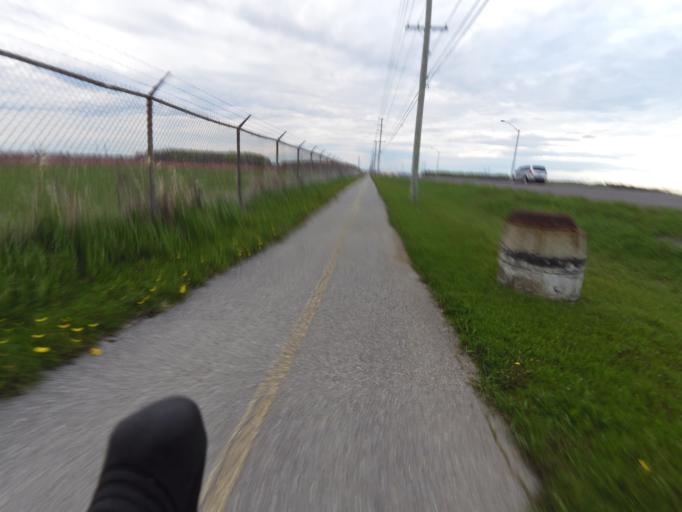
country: CA
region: Ontario
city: Bells Corners
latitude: 45.3063
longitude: -75.7680
